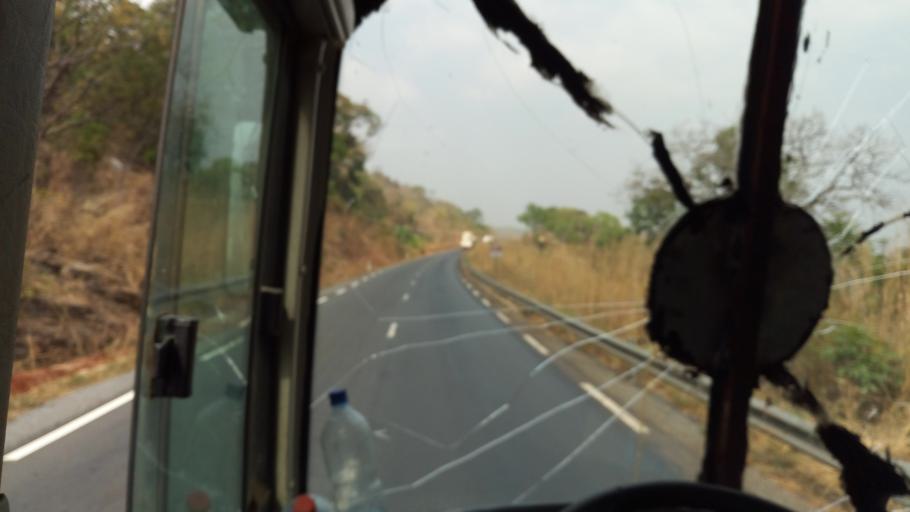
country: TG
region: Kara
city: Bafilo
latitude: 9.2407
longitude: 1.2114
